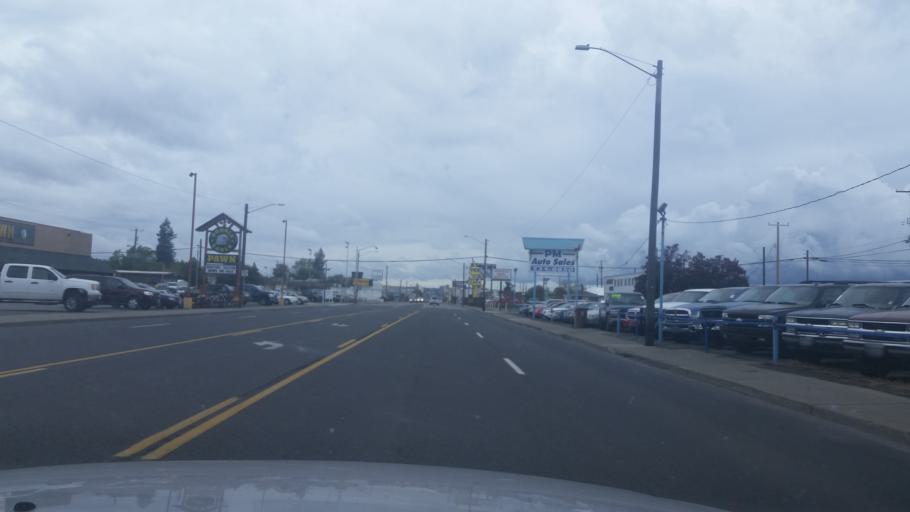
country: US
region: Washington
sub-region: Spokane County
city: Spokane
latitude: 47.6574
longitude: -117.3656
